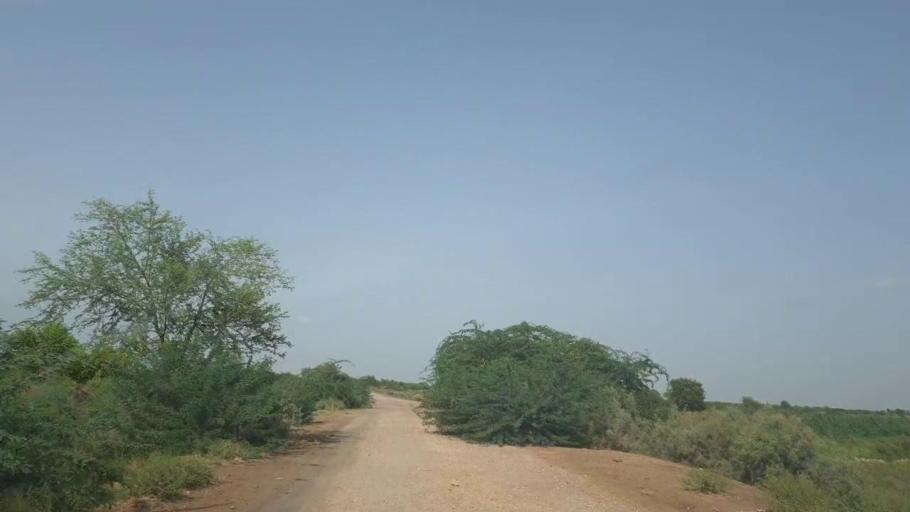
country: PK
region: Sindh
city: Tando Bago
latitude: 24.7944
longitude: 69.1489
